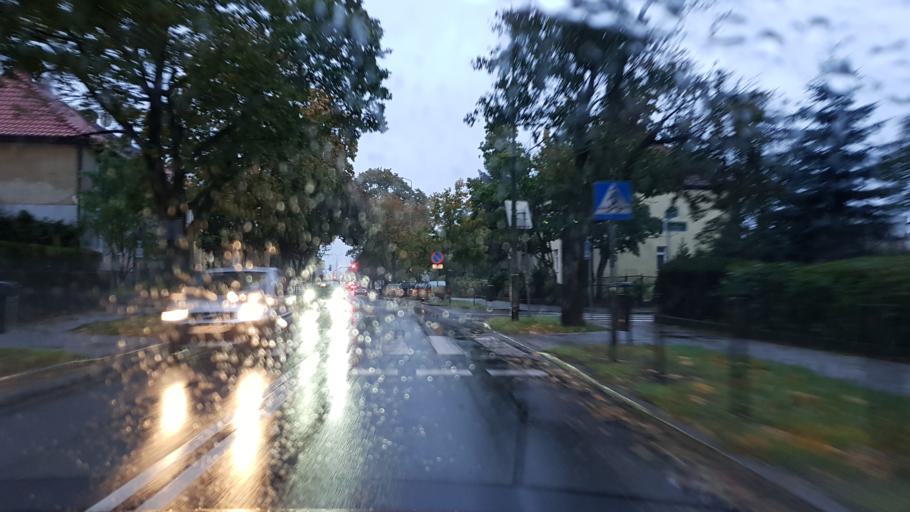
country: PL
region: West Pomeranian Voivodeship
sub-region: Szczecin
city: Szczecin
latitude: 53.4352
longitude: 14.5121
